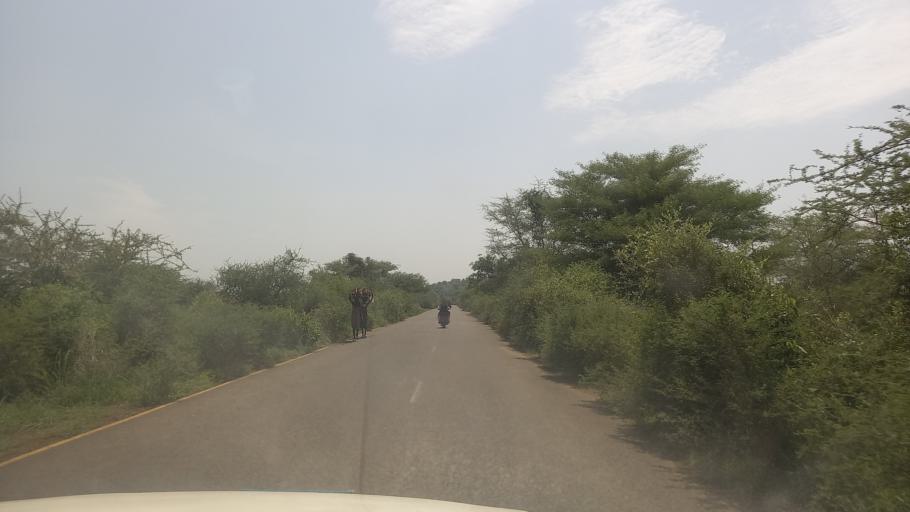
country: ET
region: Gambela
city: Gambela
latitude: 8.2813
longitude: 34.2231
